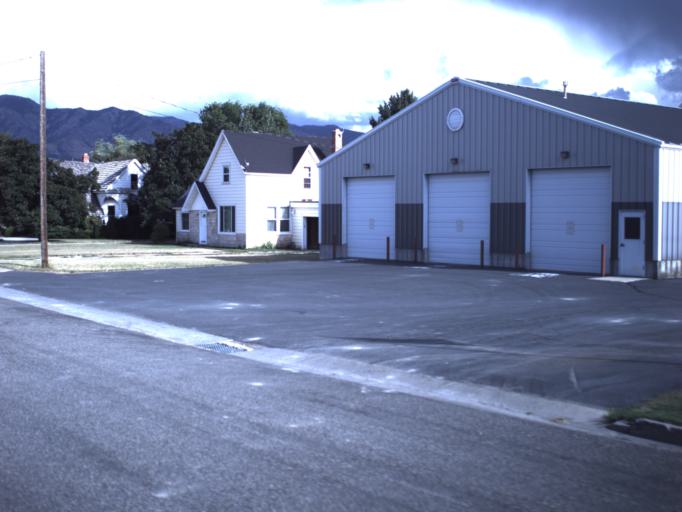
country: US
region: Utah
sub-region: Cache County
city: Lewiston
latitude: 41.9759
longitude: -111.8556
